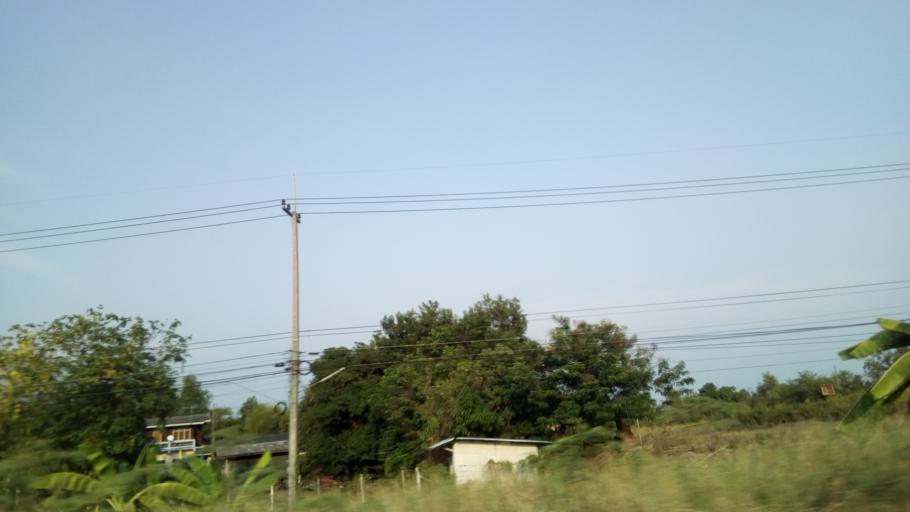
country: TH
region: Sara Buri
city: Nong Khae
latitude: 14.2613
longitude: 100.8233
